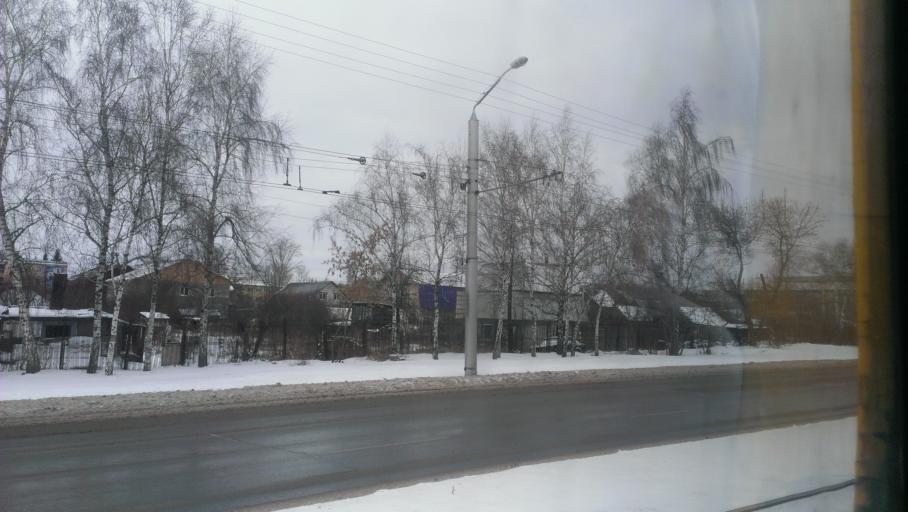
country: RU
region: Altai Krai
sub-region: Gorod Barnaulskiy
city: Barnaul
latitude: 53.3812
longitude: 83.7131
